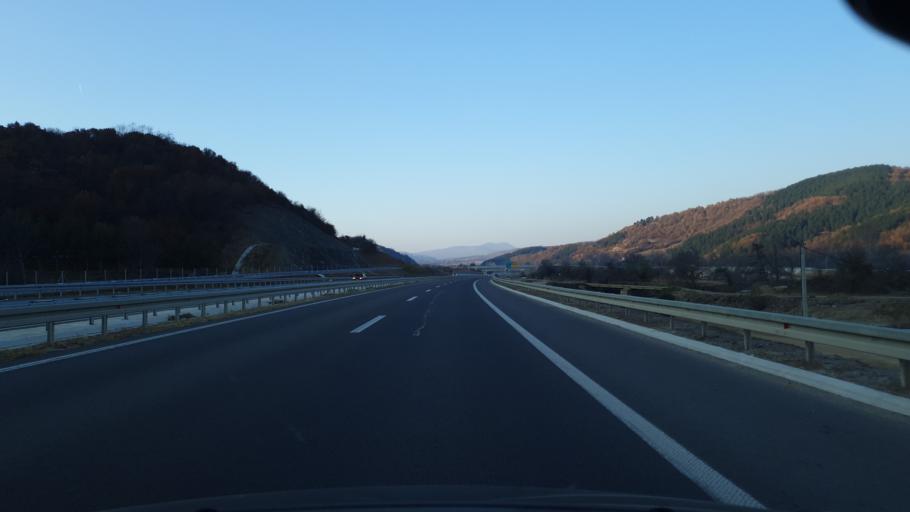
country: RS
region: Central Serbia
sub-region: Pirotski Okrug
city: Pirot
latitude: 43.1821
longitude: 22.5668
